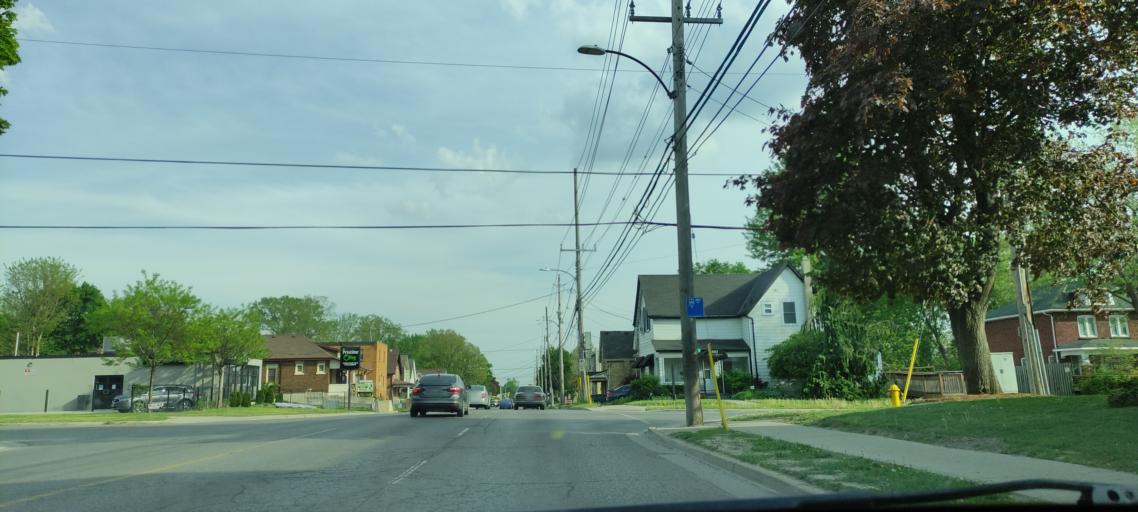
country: CA
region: Ontario
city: London
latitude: 43.0044
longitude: -81.2394
